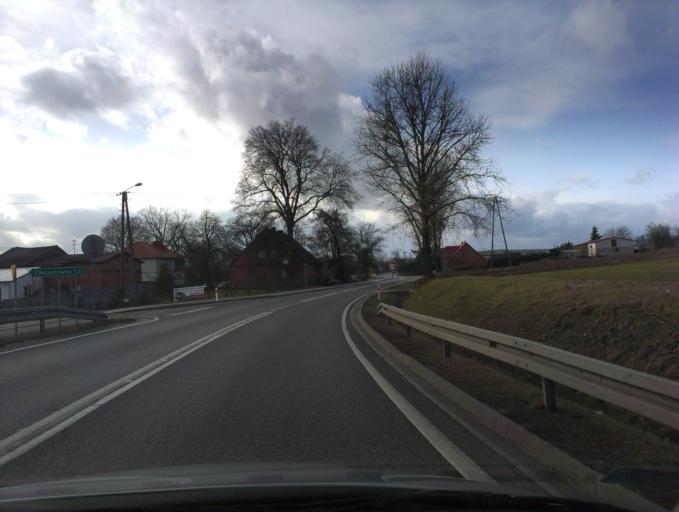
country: PL
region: Pomeranian Voivodeship
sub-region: Powiat czluchowski
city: Debrzno
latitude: 53.6255
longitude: 17.2365
